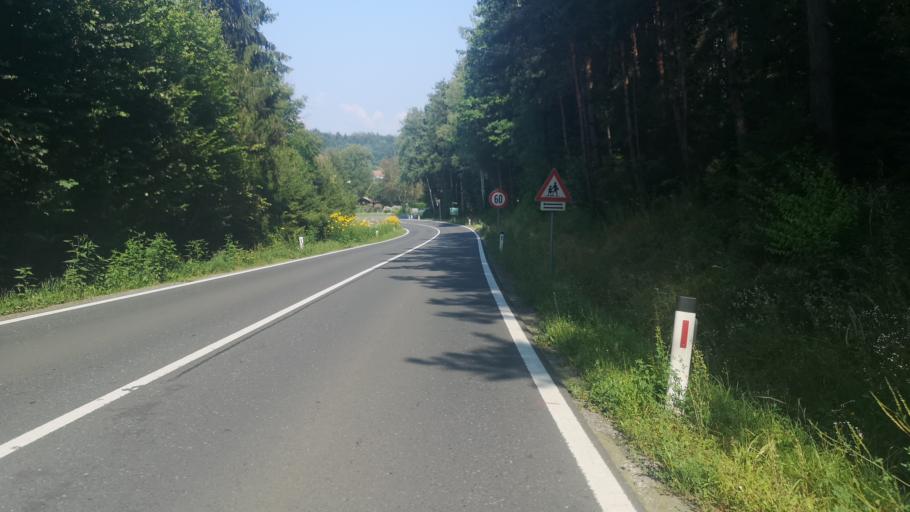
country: AT
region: Styria
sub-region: Politischer Bezirk Graz-Umgebung
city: Pirka
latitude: 46.9721
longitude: 15.3723
